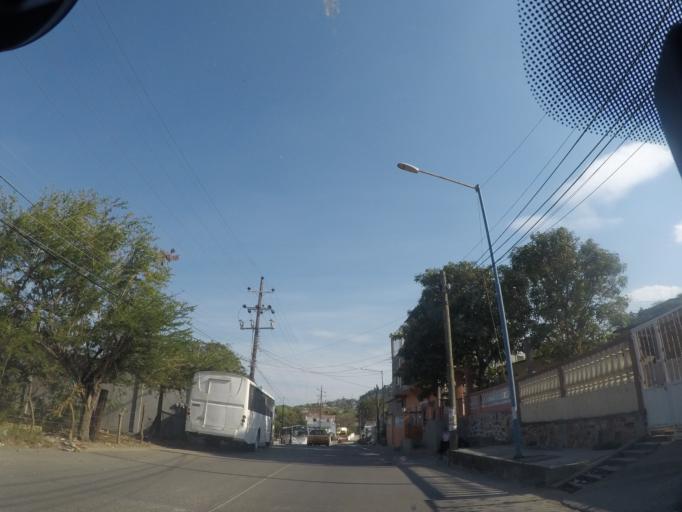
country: MX
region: Oaxaca
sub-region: Salina Cruz
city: Salina Cruz
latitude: 16.1928
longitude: -95.2022
